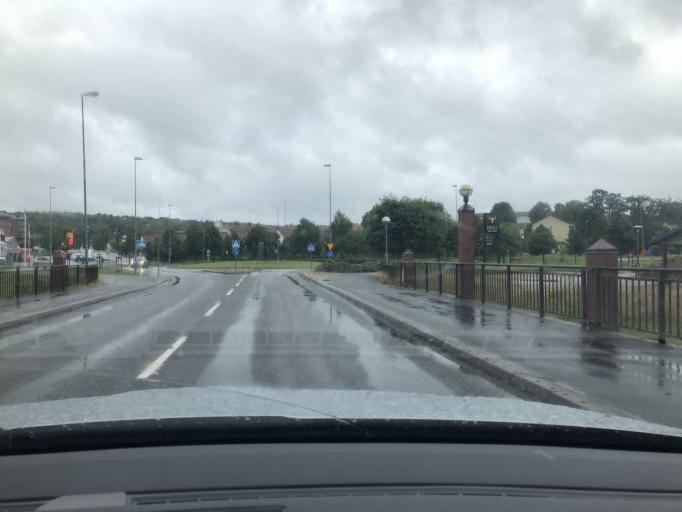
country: SE
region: Blekinge
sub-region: Olofstroms Kommun
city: Olofstroem
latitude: 56.2777
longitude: 14.5331
